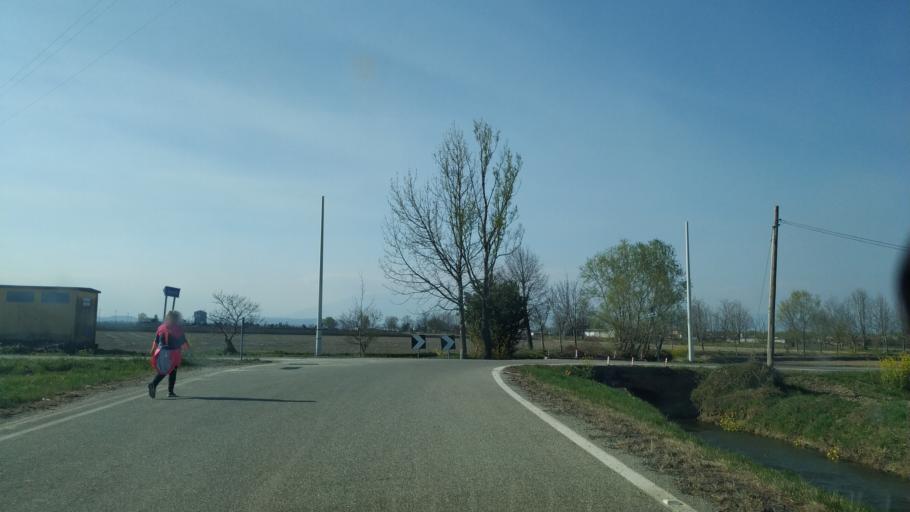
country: IT
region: Piedmont
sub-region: Provincia di Vercelli
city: San Germano Vercellese
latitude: 45.3407
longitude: 8.2515
